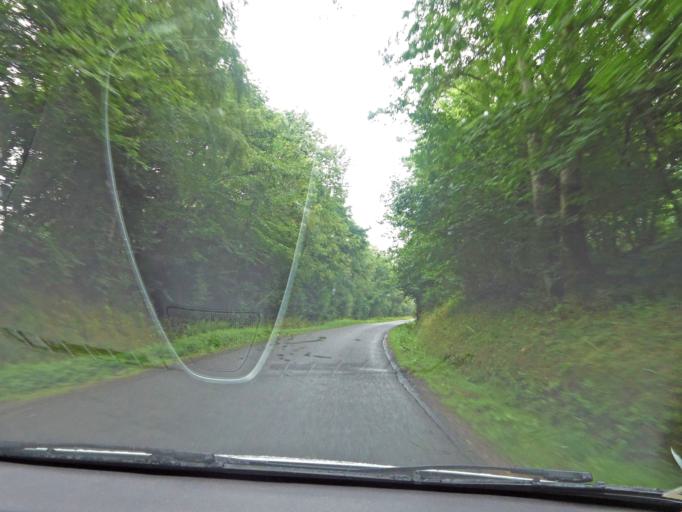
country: FR
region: Auvergne
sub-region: Departement du Puy-de-Dome
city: Saint-Genes-Champanelle
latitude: 45.7296
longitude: 2.9817
